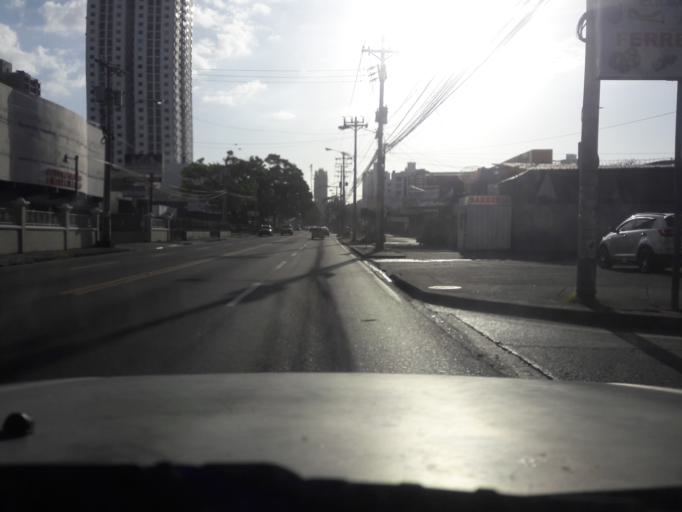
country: PA
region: Panama
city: Panama
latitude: 9.0126
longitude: -79.5021
